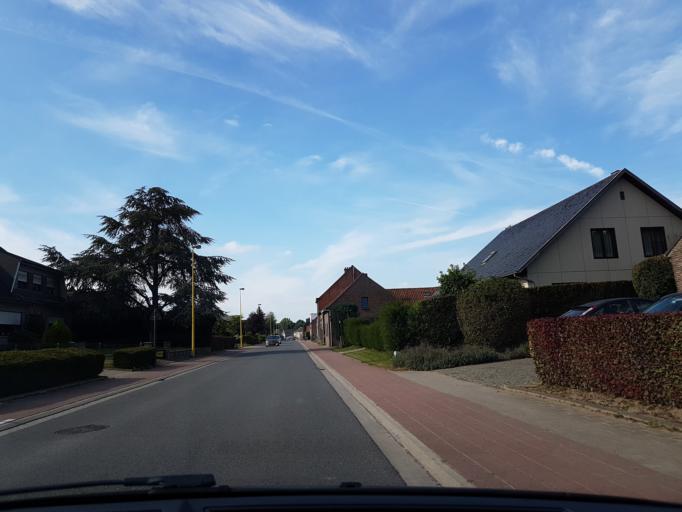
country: BE
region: Flanders
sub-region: Provincie Vlaams-Brabant
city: Grimbergen
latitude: 50.9703
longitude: 4.3924
